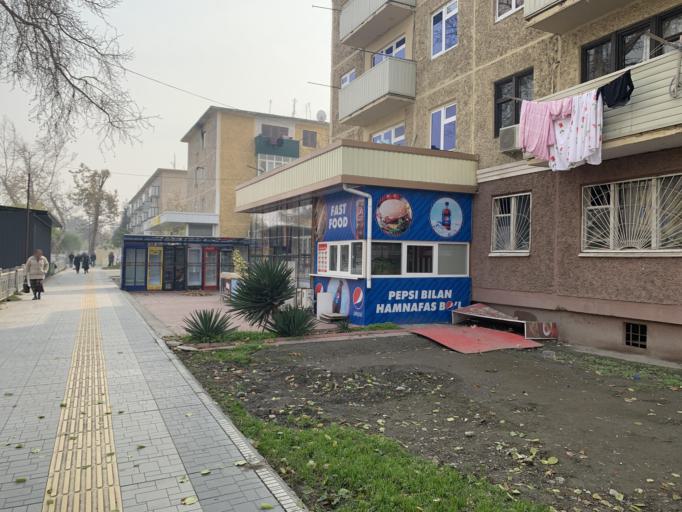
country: UZ
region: Fergana
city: Qo`qon
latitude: 40.5445
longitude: 70.9322
